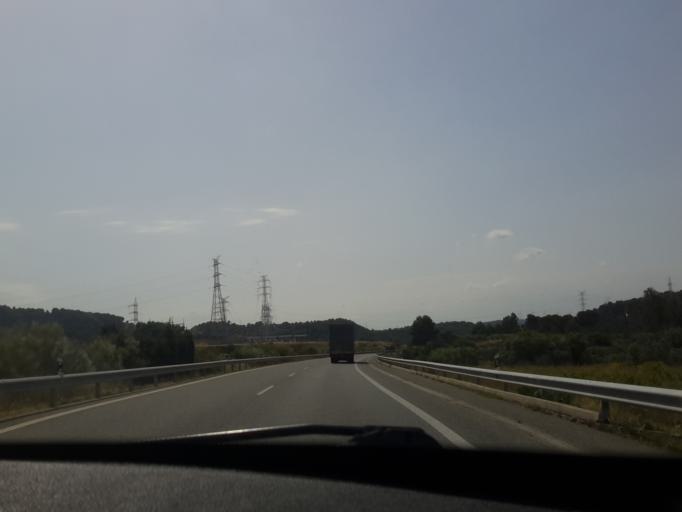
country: ES
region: Catalonia
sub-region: Provincia de Tarragona
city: Montblanc
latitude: 41.4044
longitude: 1.1357
